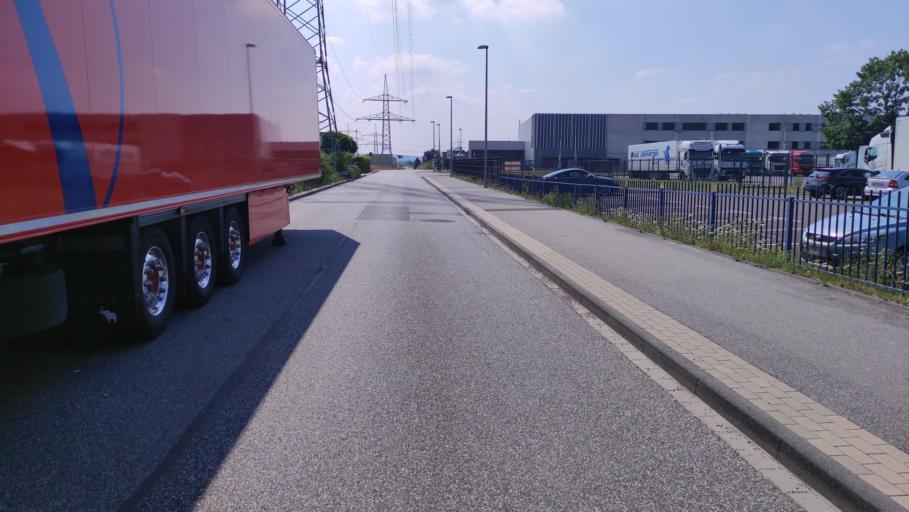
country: DE
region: North Rhine-Westphalia
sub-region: Regierungsbezirk Koln
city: Alfter
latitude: 50.7562
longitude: 7.0222
